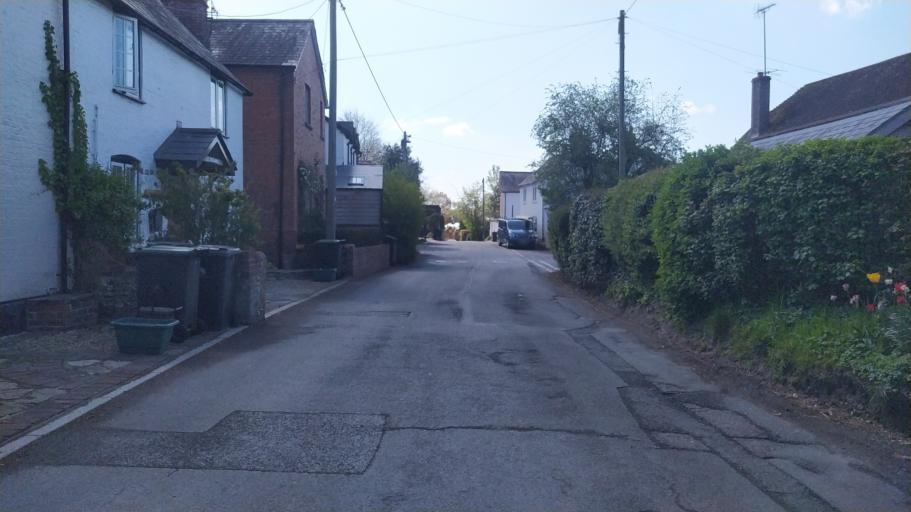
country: GB
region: England
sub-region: Dorset
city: Manston
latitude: 50.9115
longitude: -2.2362
